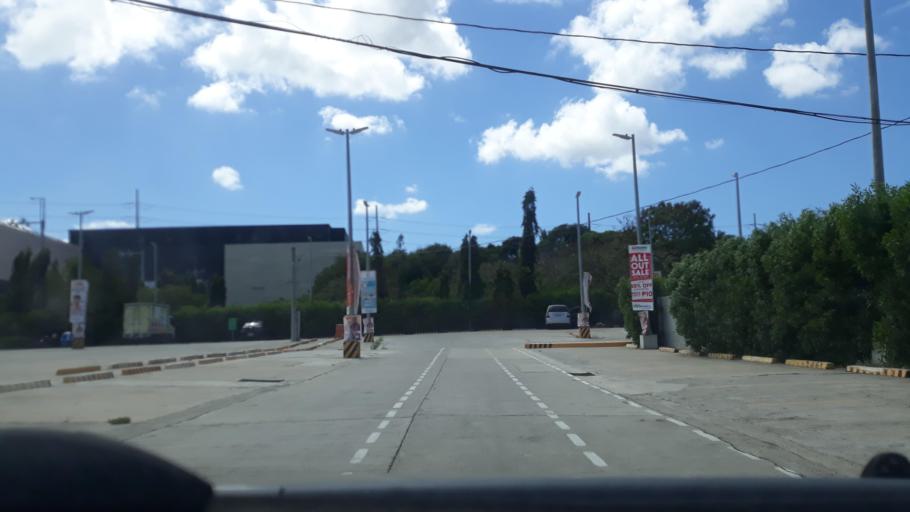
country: PH
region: Calabarzon
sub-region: Province of Cavite
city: Dasmarinas
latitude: 14.3183
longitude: 120.9458
